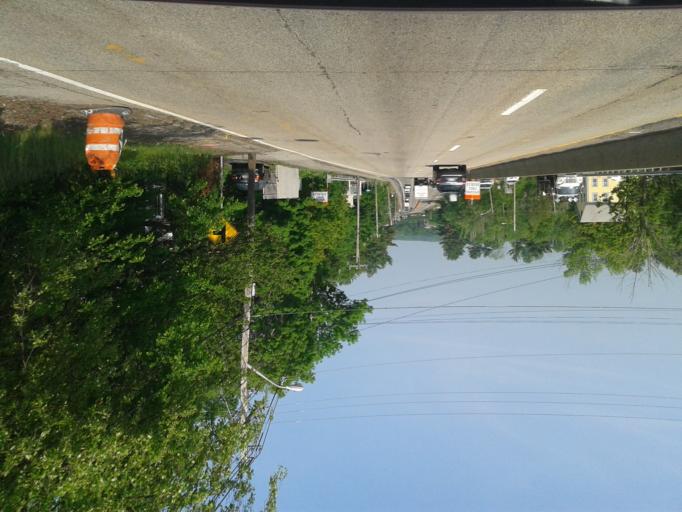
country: US
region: Massachusetts
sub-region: Worcester County
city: Southborough
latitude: 42.2946
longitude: -71.5062
